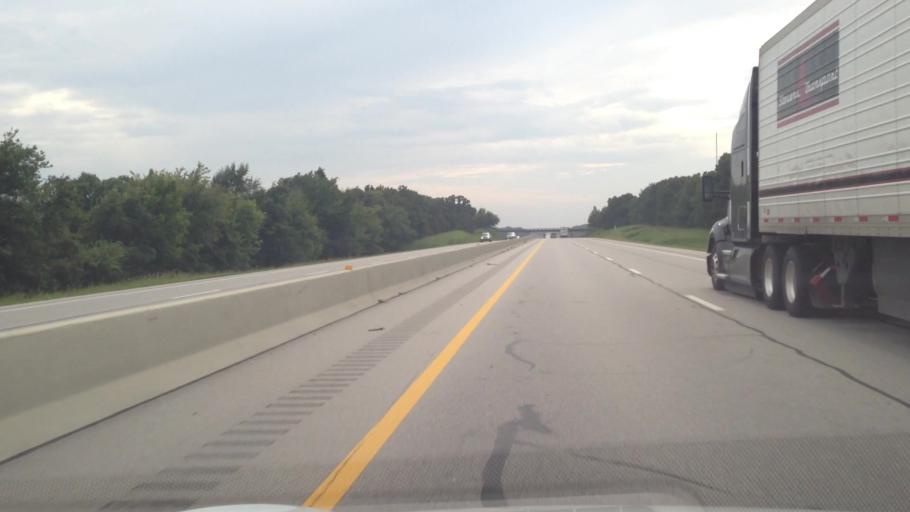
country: US
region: Kansas
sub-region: Cherokee County
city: Baxter Springs
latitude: 36.9313
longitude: -94.7227
